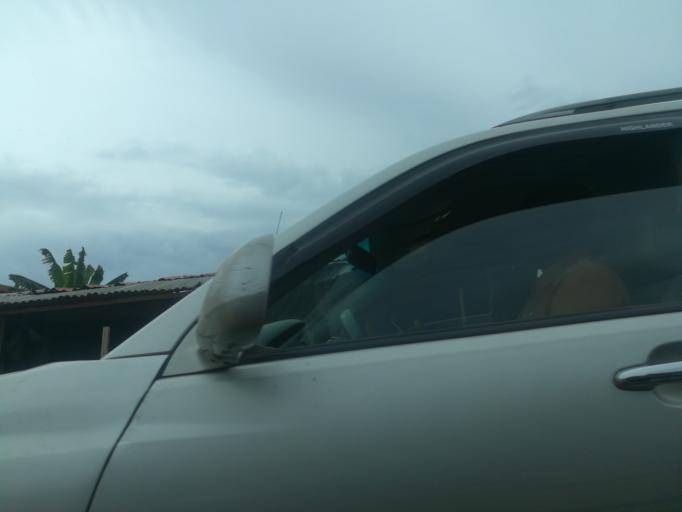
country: NG
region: Oyo
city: Ibadan
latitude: 7.3925
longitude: 3.9513
